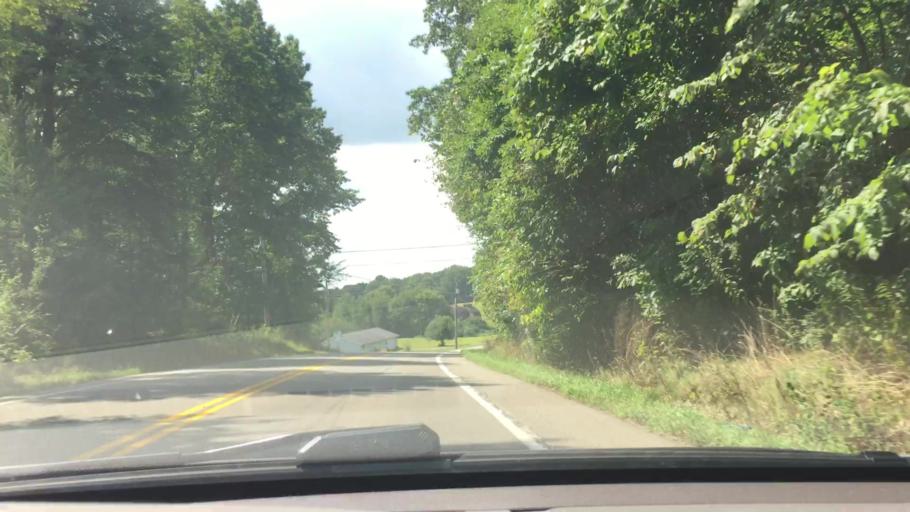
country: US
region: Pennsylvania
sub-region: Mercer County
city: Mercer
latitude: 41.1406
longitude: -80.1942
